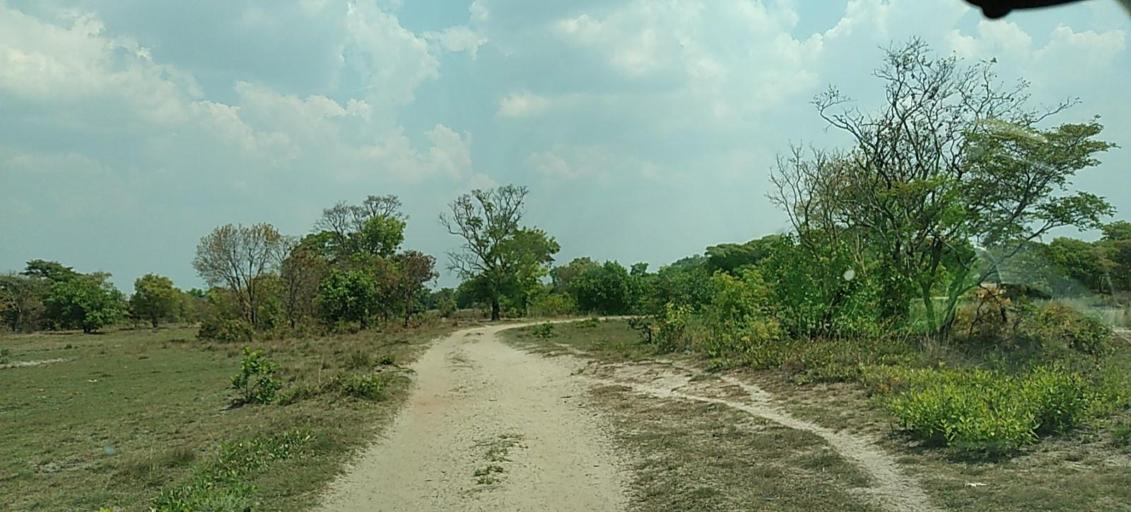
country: ZM
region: North-Western
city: Kabompo
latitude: -13.3560
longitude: 23.8947
